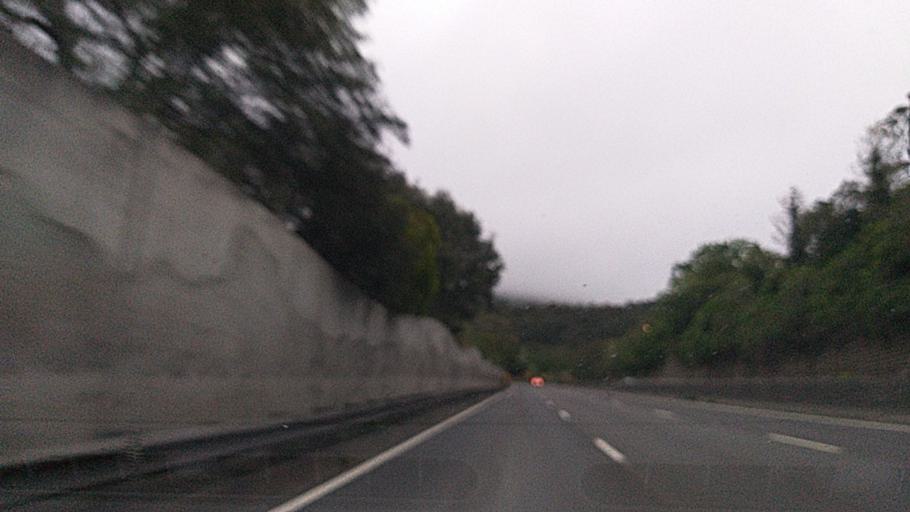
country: AU
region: New South Wales
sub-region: Wollongong
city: Mount Ousley
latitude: -34.4018
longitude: 150.8722
